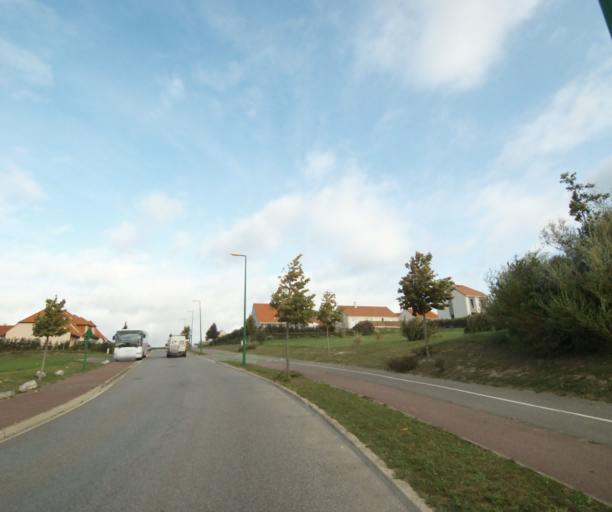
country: FR
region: Nord-Pas-de-Calais
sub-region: Departement du Pas-de-Calais
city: Etaples
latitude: 50.5108
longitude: 1.6556
